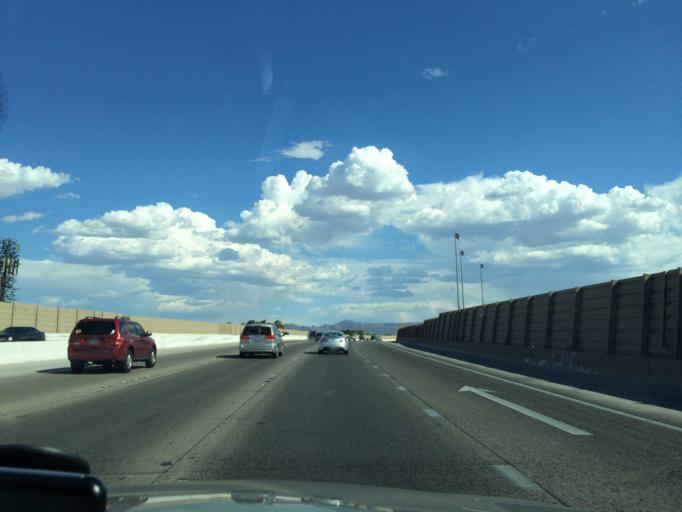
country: US
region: Nevada
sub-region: Clark County
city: Winchester
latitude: 36.1235
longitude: -115.0845
